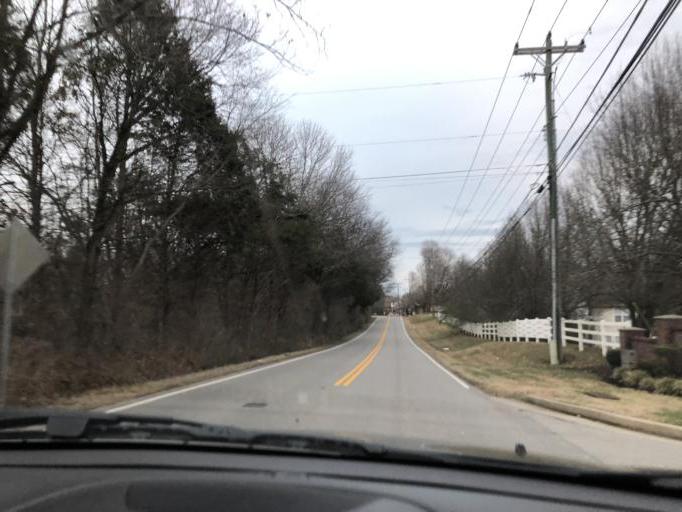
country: US
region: Tennessee
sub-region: Wilson County
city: Green Hill
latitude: 36.1889
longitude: -86.5919
